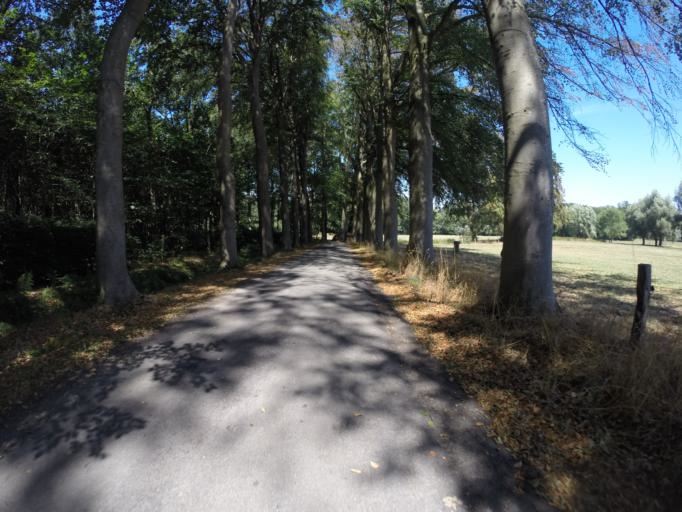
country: BE
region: Flanders
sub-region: Provincie Oost-Vlaanderen
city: Knesselare
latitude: 51.1017
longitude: 3.3924
